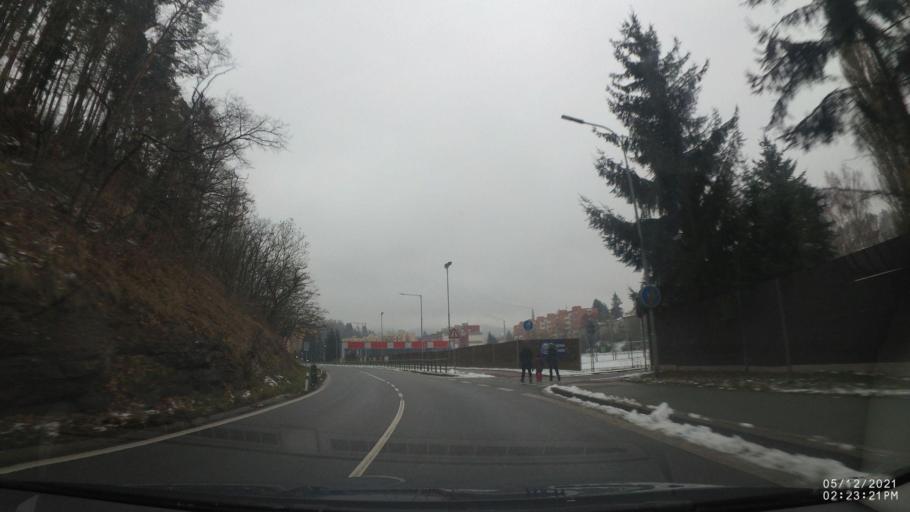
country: CZ
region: Kralovehradecky
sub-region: Okres Nachod
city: Nachod
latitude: 50.4253
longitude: 16.1598
